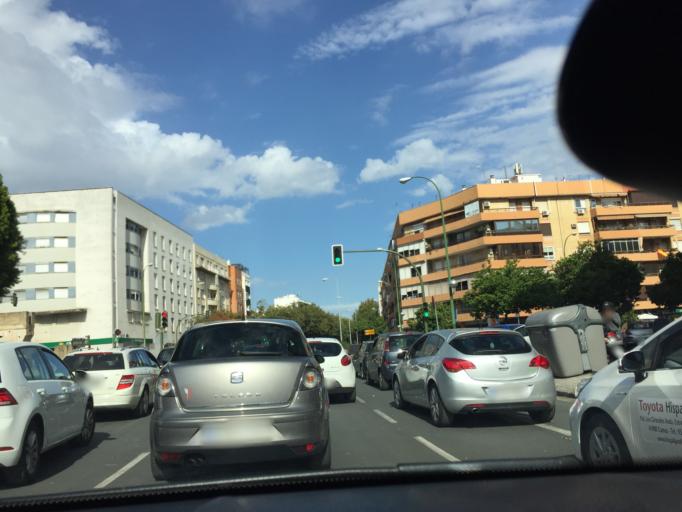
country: ES
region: Andalusia
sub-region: Provincia de Sevilla
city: Sevilla
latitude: 37.3878
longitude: -5.9826
